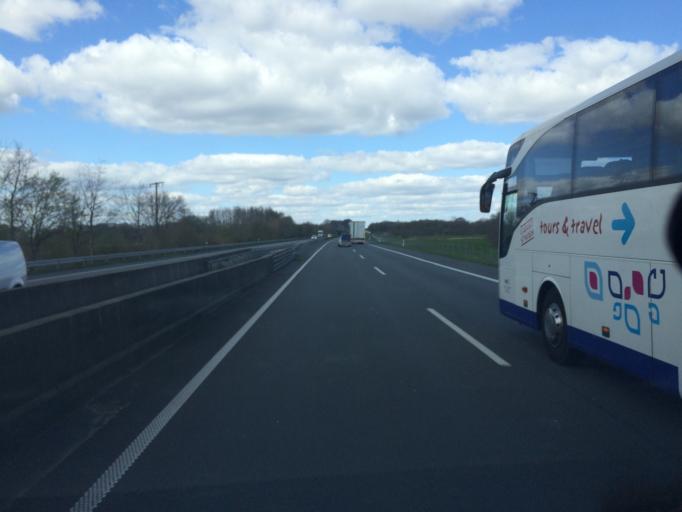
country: DE
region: North Rhine-Westphalia
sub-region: Regierungsbezirk Munster
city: Heek
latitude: 52.1438
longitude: 7.0901
